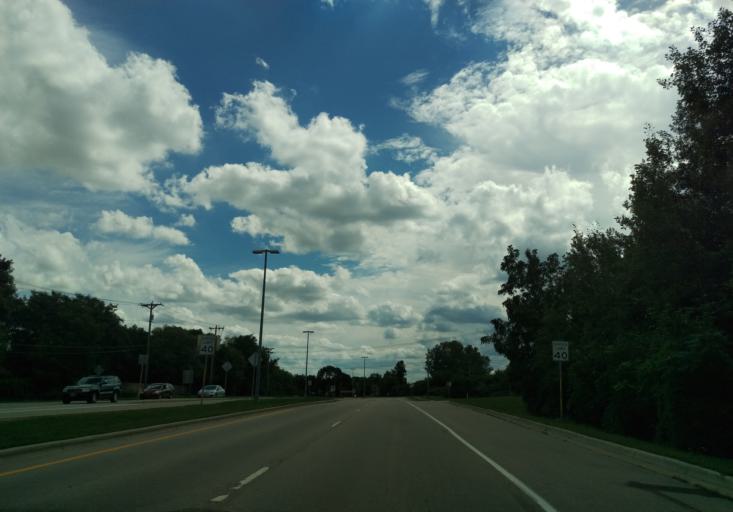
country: US
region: Wisconsin
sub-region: Dane County
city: Maple Bluff
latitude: 43.1426
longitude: -89.3931
